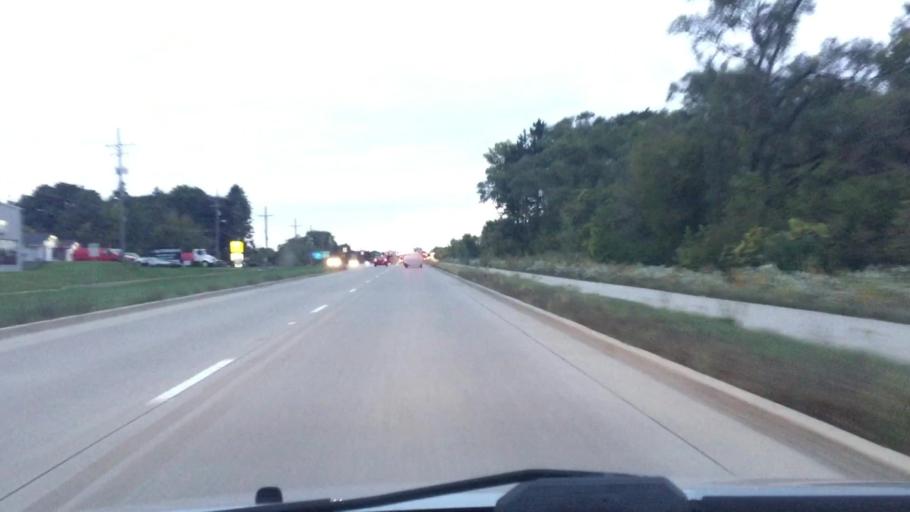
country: US
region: Illinois
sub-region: McHenry County
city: Algonquin
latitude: 42.2056
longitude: -88.2864
